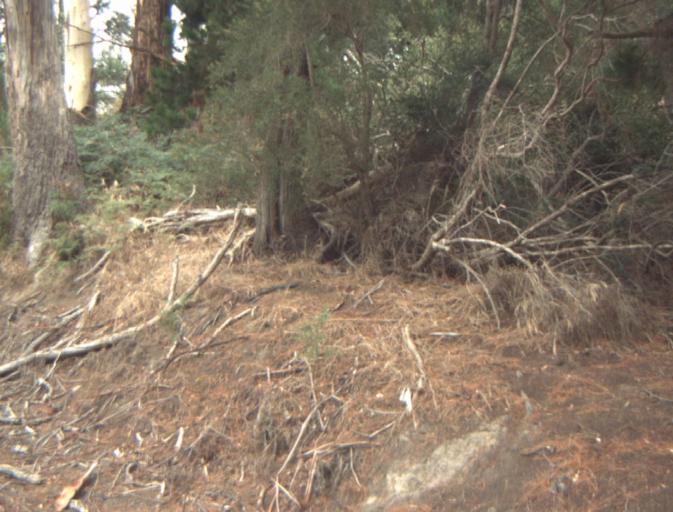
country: AU
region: Tasmania
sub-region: Launceston
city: Mayfield
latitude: -41.2489
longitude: 147.2001
